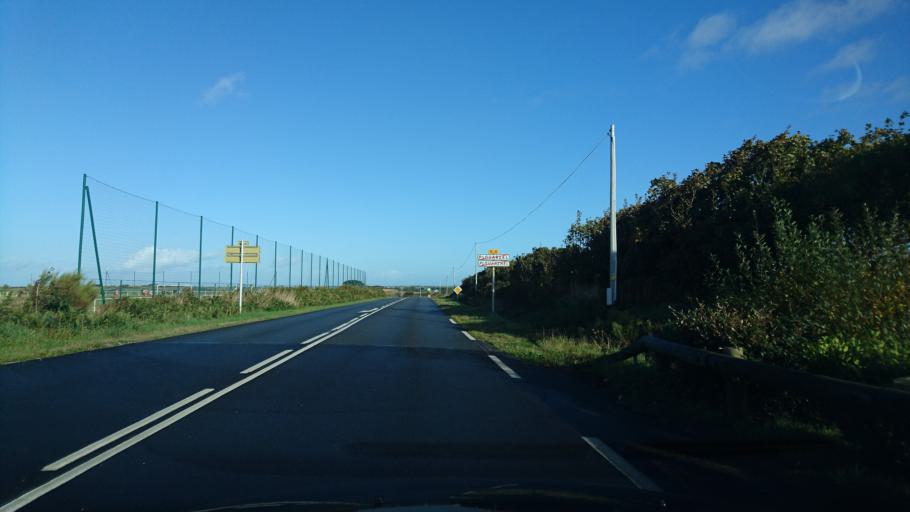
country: FR
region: Brittany
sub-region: Departement du Finistere
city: Plouarzel
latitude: 48.4349
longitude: -4.7153
